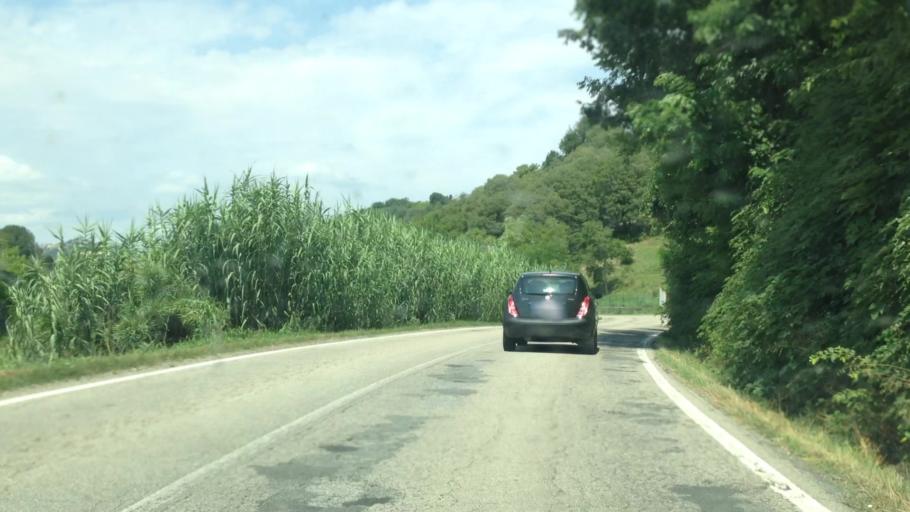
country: IT
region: Piedmont
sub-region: Provincia di Asti
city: Montiglio
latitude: 45.0740
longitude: 8.1016
